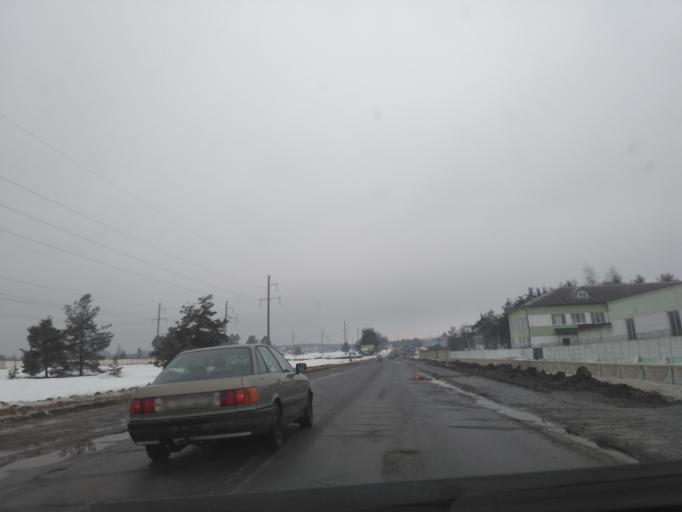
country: BY
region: Minsk
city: Horad Barysaw
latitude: 54.1988
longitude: 28.5004
